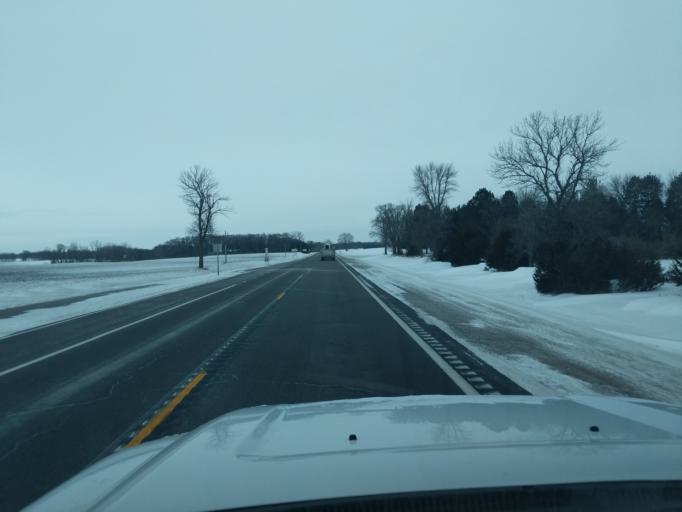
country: US
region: Minnesota
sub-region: Redwood County
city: Redwood Falls
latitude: 44.5775
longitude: -94.9946
